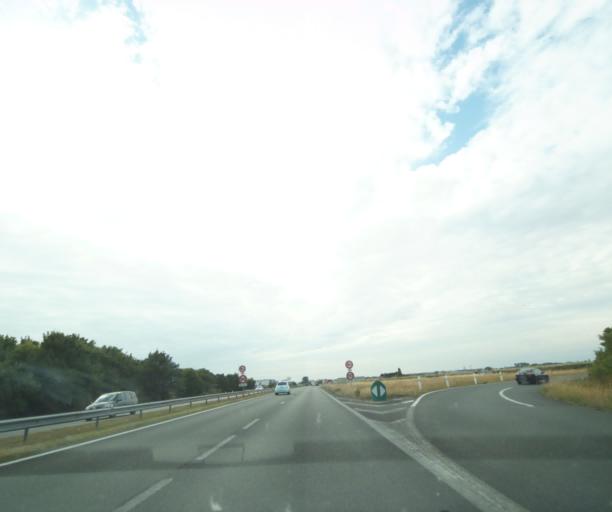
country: FR
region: Poitou-Charentes
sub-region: Departement de la Charente-Maritime
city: Angoulins
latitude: 46.1050
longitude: -1.0962
